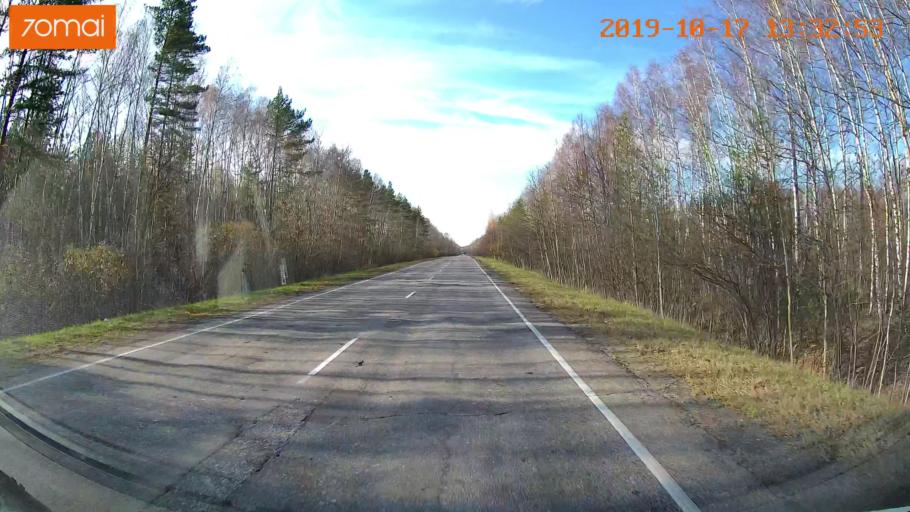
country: RU
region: Vladimir
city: Velikodvorskiy
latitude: 55.1395
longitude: 40.7545
